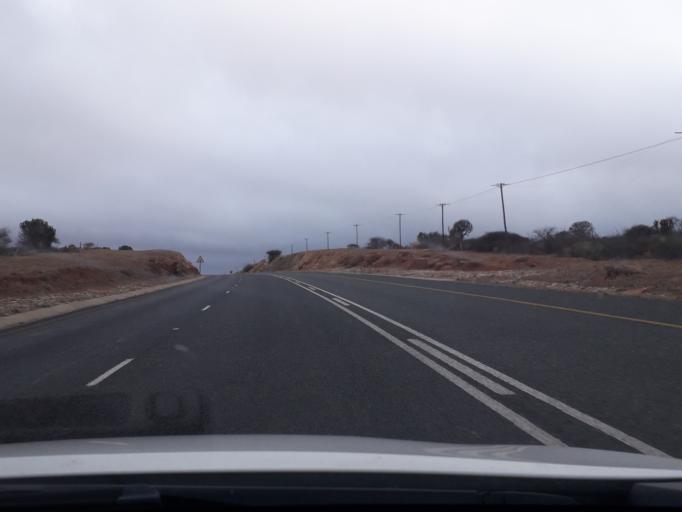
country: ZA
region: Limpopo
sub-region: Vhembe District Municipality
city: Louis Trichardt
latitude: -23.4383
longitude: 29.7459
